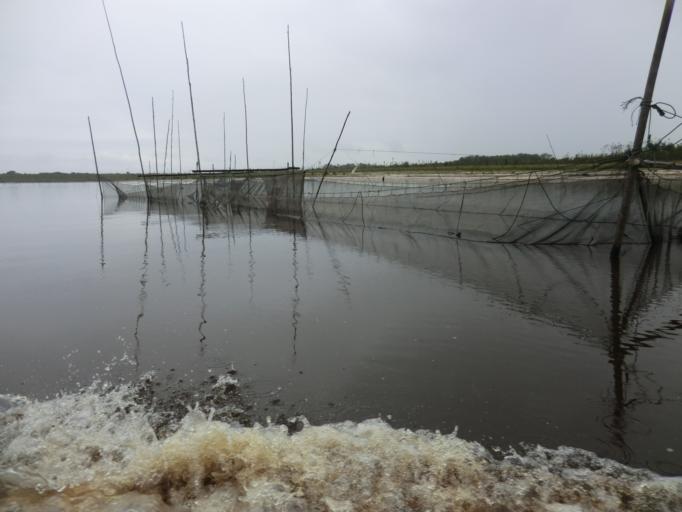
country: MY
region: Sarawak
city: Simanggang
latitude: 0.9644
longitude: 112.1730
